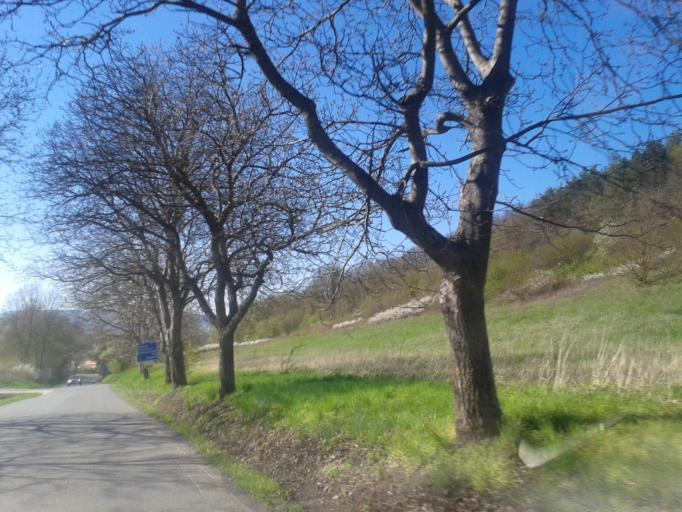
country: CZ
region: Central Bohemia
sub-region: Okres Beroun
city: Beroun
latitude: 49.9176
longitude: 14.0765
